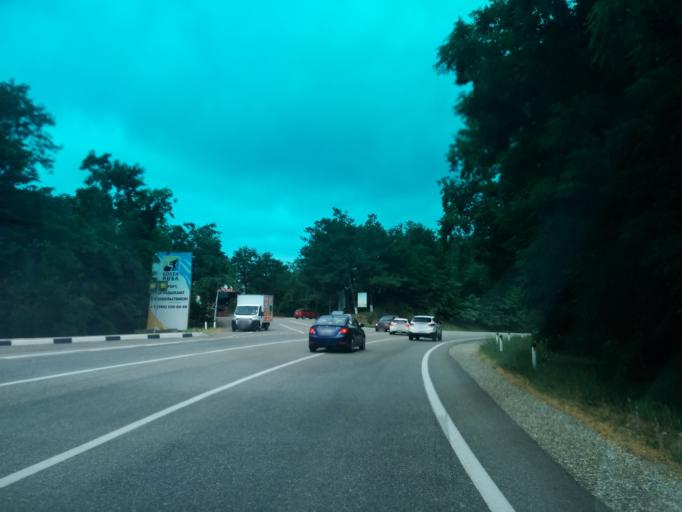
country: RU
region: Krasnodarskiy
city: Nebug
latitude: 44.1744
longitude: 38.9633
